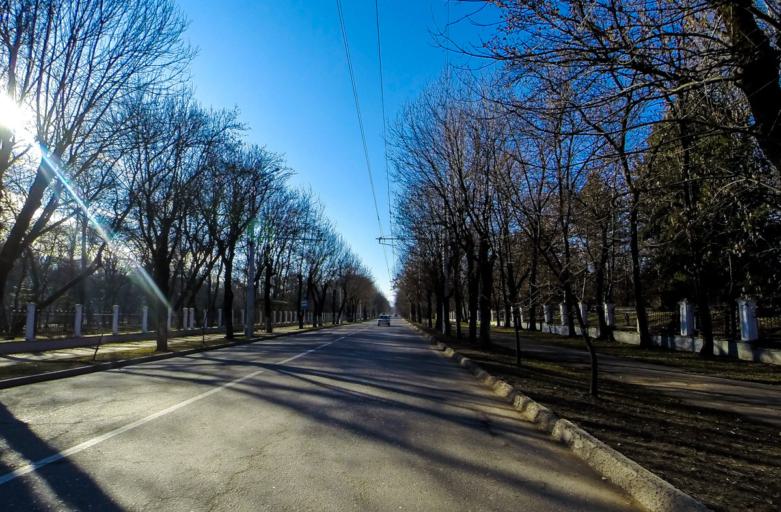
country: RU
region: Kabardino-Balkariya
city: Vol'nyy Aul
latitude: 43.4652
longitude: 43.5898
